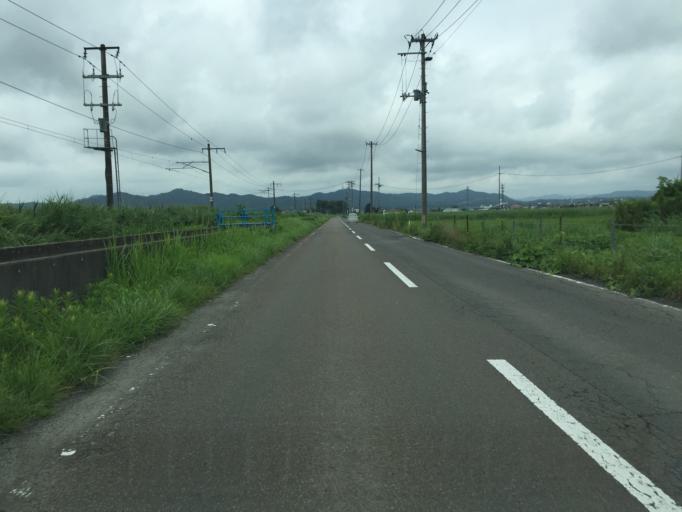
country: JP
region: Miyagi
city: Watari
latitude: 38.0265
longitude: 140.8747
